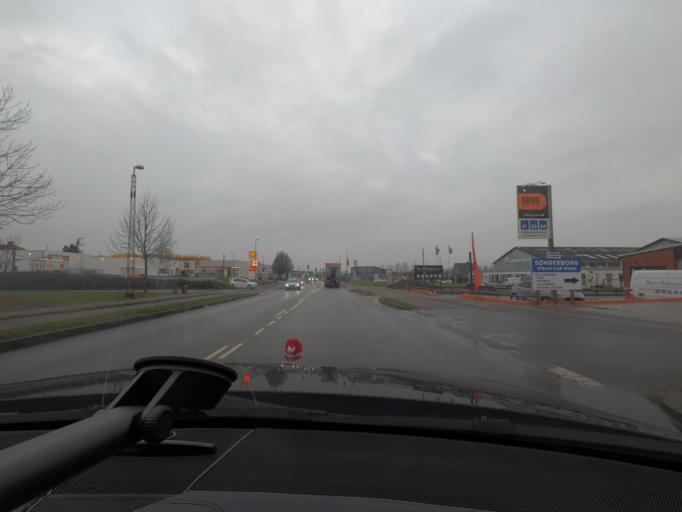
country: DK
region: South Denmark
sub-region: Sonderborg Kommune
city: Sonderborg
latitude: 54.9186
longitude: 9.8101
